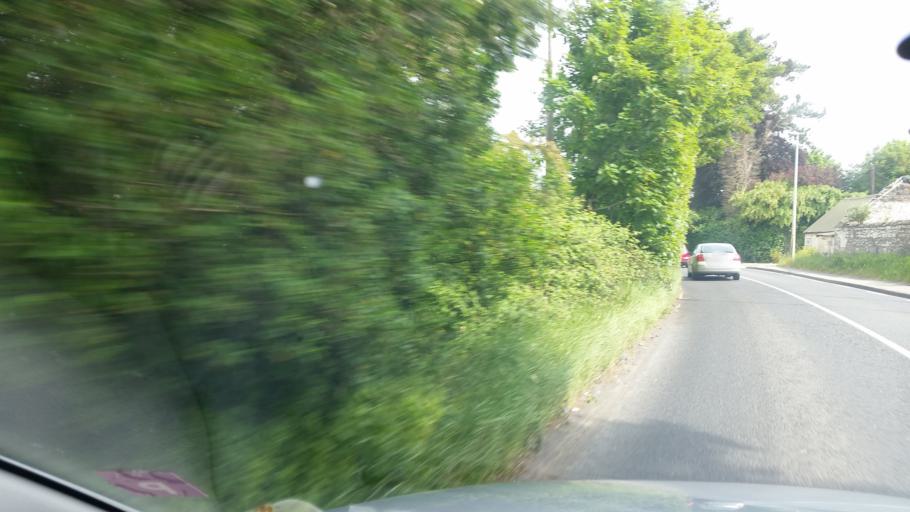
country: IE
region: Leinster
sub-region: Dublin City
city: Finglas
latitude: 53.4107
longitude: -6.3065
